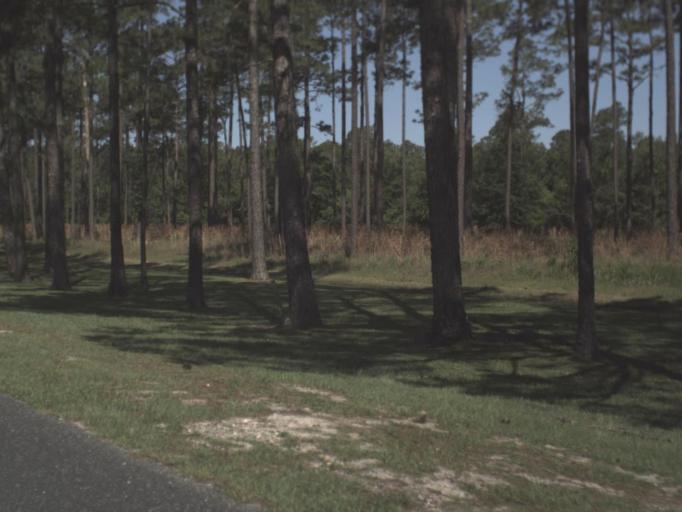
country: US
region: Florida
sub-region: Union County
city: Lake Butler
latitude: 30.2155
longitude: -82.3761
